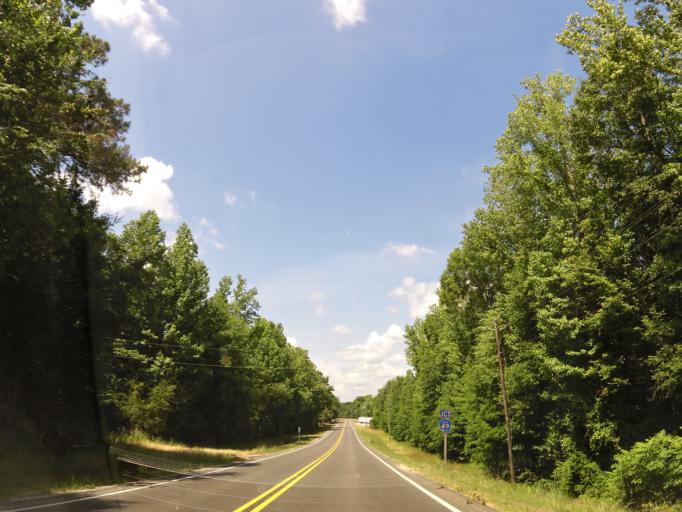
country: US
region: Alabama
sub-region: Marion County
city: Guin
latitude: 33.9331
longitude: -88.0162
